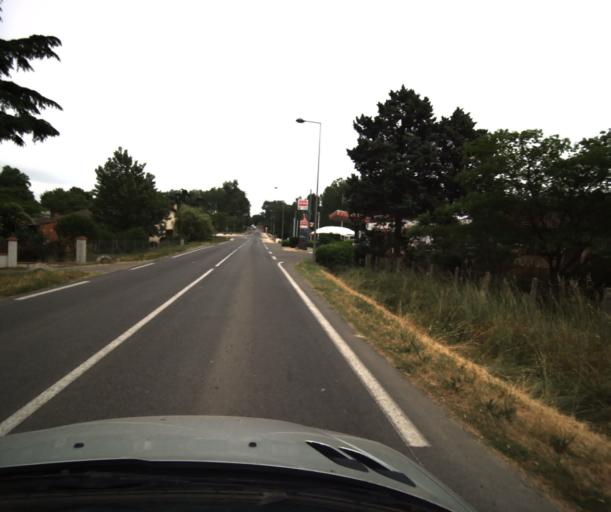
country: FR
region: Midi-Pyrenees
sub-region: Departement du Tarn-et-Garonne
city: Saint-Nicolas-de-la-Grave
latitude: 44.0310
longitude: 1.0369
